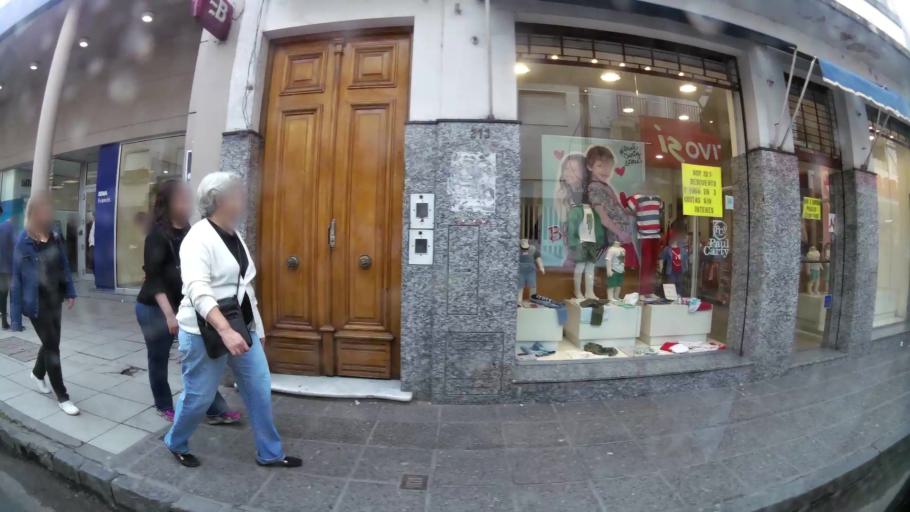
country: AR
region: Buenos Aires
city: San Nicolas de los Arroyos
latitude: -33.3307
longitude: -60.2190
